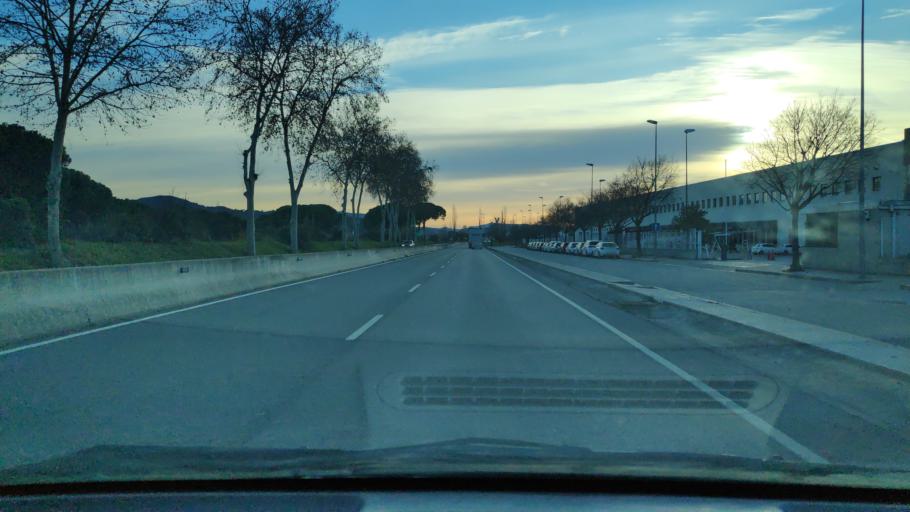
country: ES
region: Catalonia
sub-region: Provincia de Barcelona
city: Montmelo
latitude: 41.5679
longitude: 2.2671
